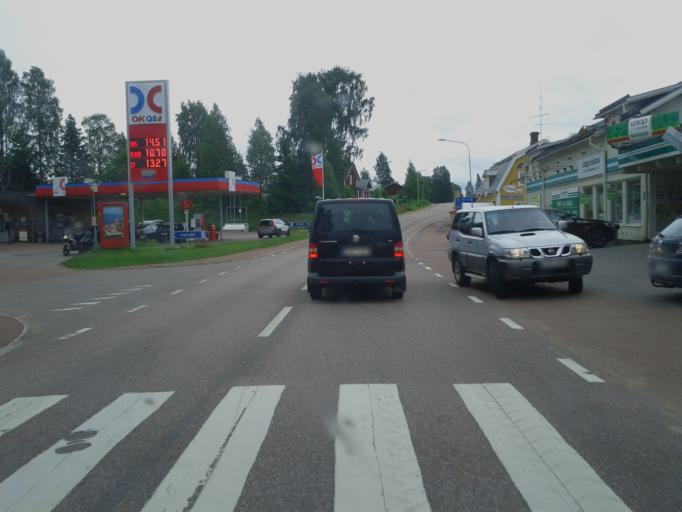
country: NO
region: Hedmark
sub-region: Trysil
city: Innbygda
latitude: 61.6932
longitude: 13.1407
